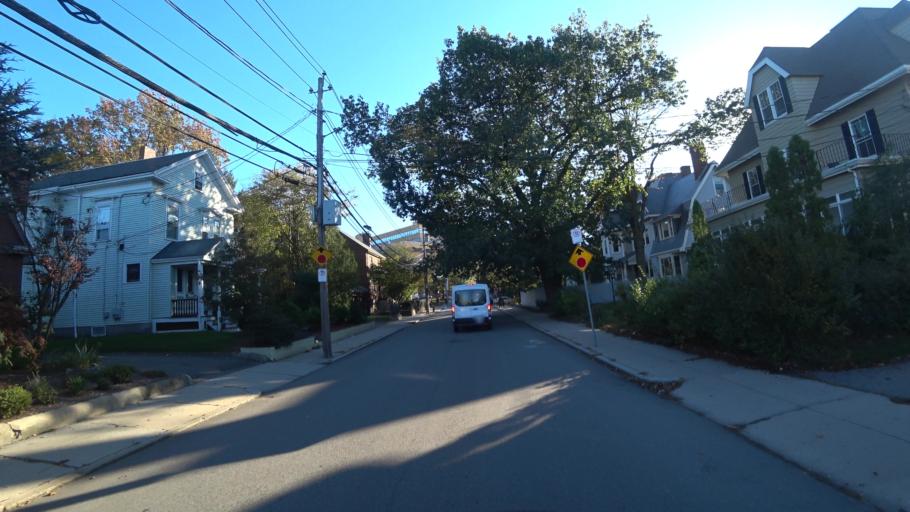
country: US
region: Massachusetts
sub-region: Norfolk County
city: Brookline
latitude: 42.3509
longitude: -71.1475
